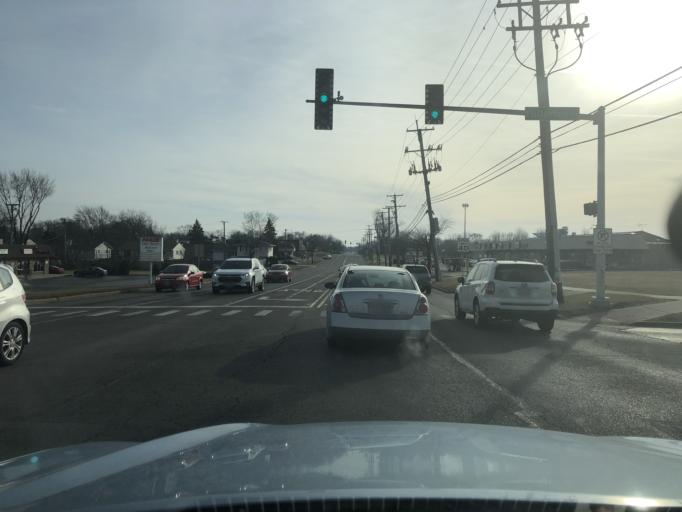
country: US
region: Illinois
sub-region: DuPage County
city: Glendale Heights
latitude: 41.9176
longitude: -88.0815
